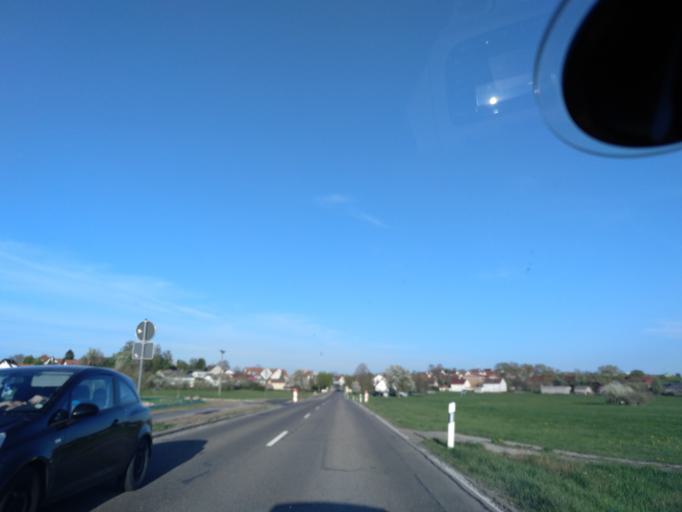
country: DE
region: Baden-Wuerttemberg
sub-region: Regierungsbezirk Stuttgart
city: Crailsheim
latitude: 49.1393
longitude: 10.0149
